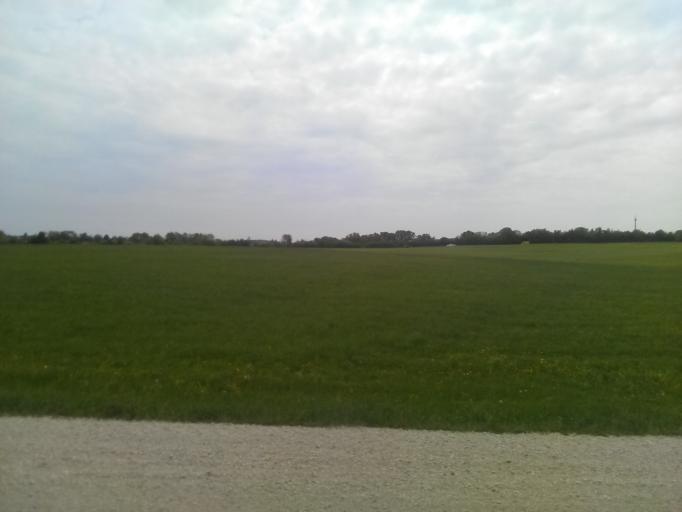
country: DE
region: Bavaria
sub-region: Upper Franconia
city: Kleinsendelbach
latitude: 49.5709
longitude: 11.1858
